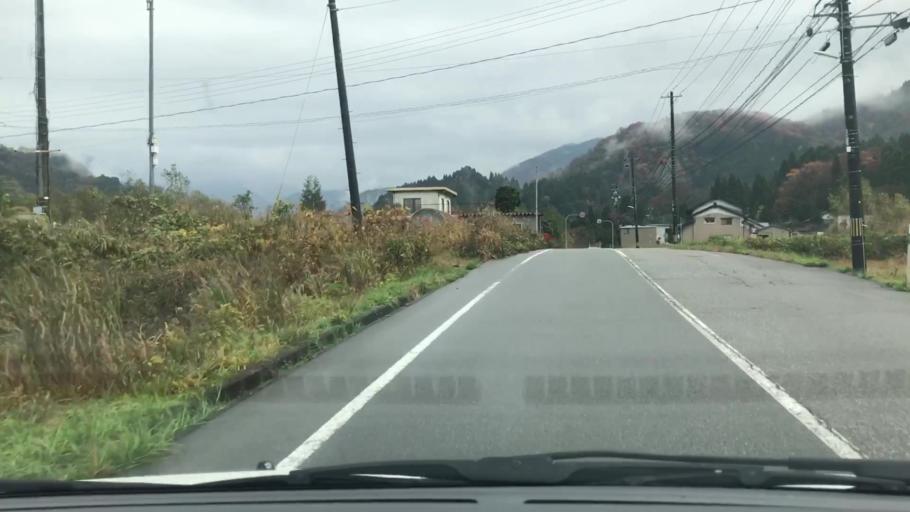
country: JP
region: Toyama
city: Kamiichi
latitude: 36.5702
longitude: 137.3569
